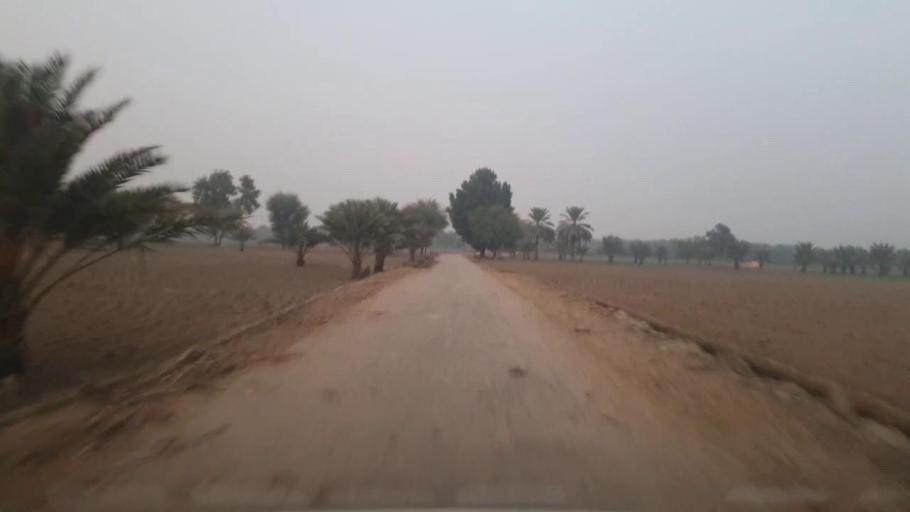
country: PK
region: Sindh
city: Gambat
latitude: 27.3455
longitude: 68.6118
